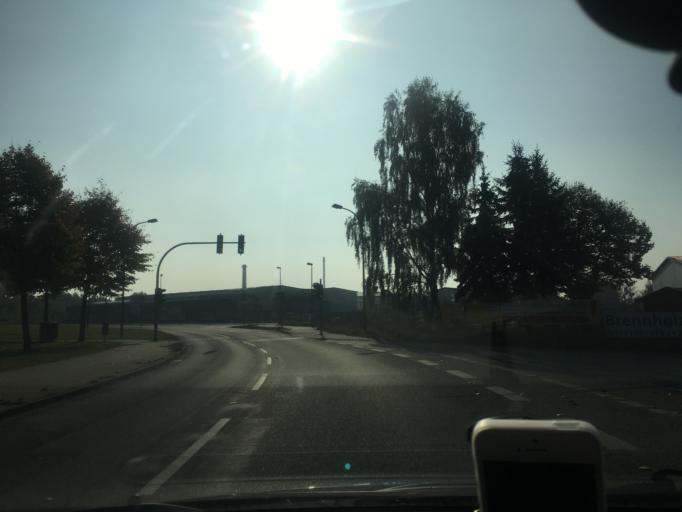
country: DE
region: Mecklenburg-Vorpommern
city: Hagenow
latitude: 53.4253
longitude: 11.1881
